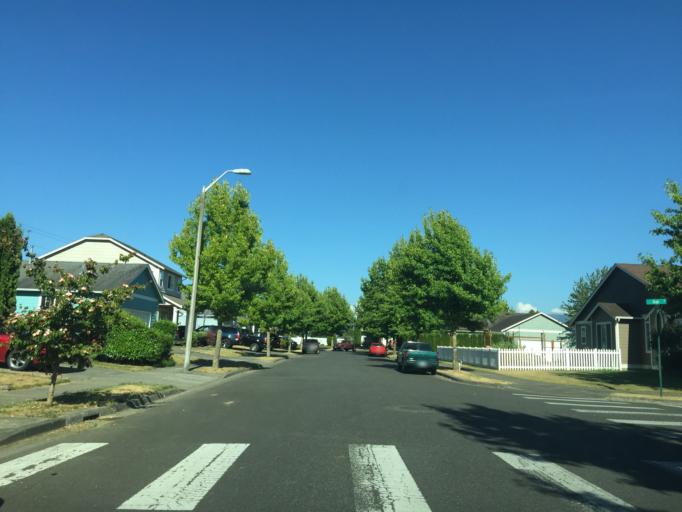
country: US
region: Washington
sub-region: Whatcom County
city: Lynden
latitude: 48.9637
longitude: -122.4262
